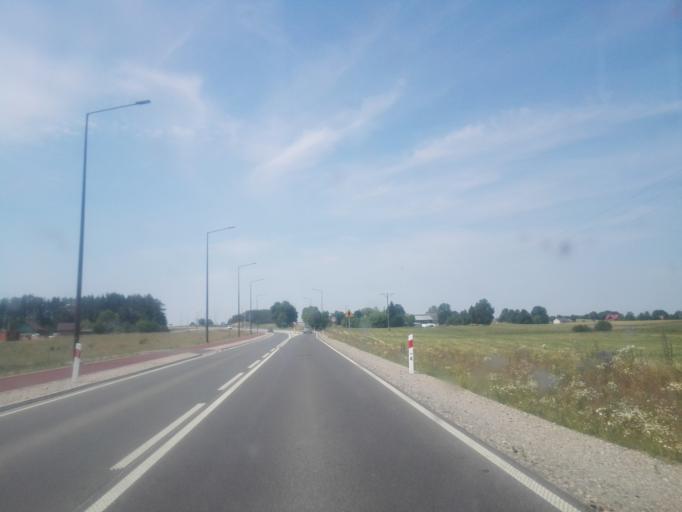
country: PL
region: Podlasie
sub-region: Powiat sejnenski
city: Krasnopol
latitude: 54.1081
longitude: 23.2580
